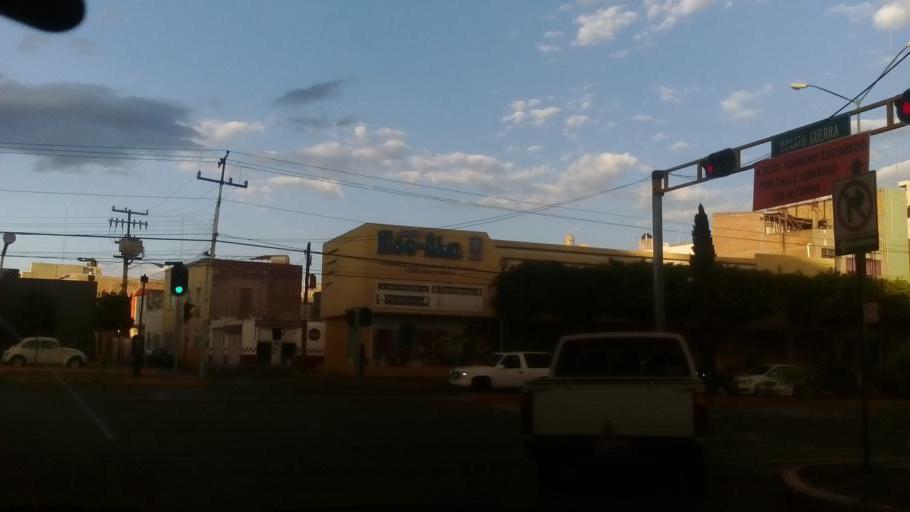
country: MX
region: Guanajuato
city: Leon
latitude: 21.1239
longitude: -101.6786
